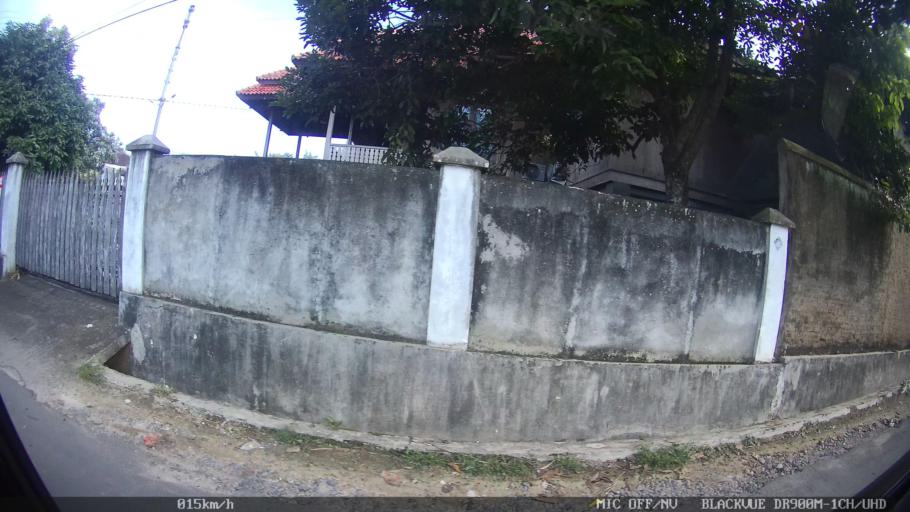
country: ID
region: Lampung
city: Kedaton
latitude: -5.3797
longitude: 105.2349
